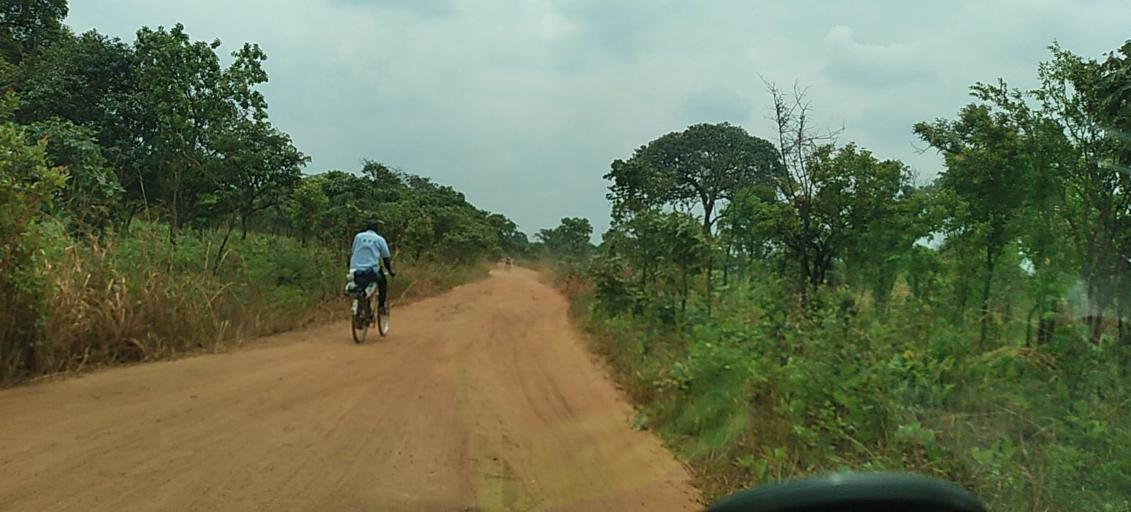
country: ZM
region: North-Western
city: Kansanshi
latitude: -12.0666
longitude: 26.3528
